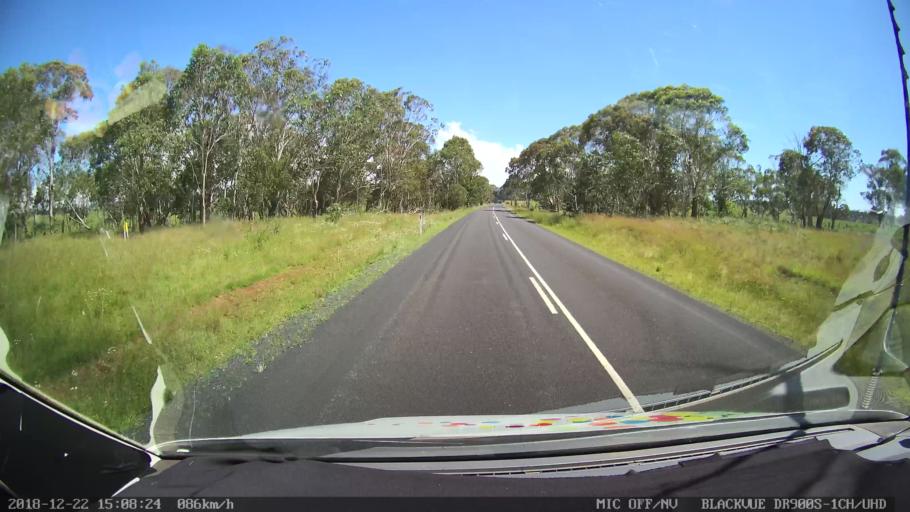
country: AU
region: New South Wales
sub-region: Bellingen
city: Dorrigo
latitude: -30.3119
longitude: 152.4139
